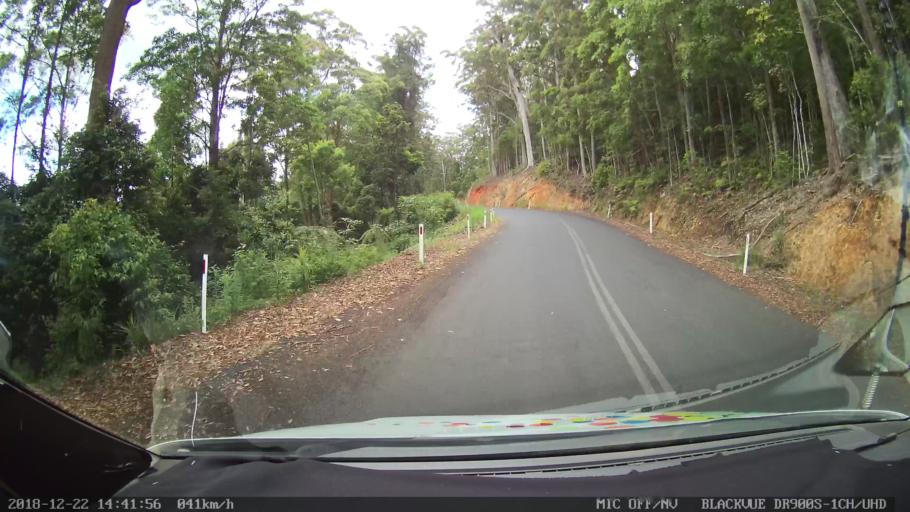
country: AU
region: New South Wales
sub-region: Bellingen
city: Dorrigo
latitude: -30.1561
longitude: 152.5865
